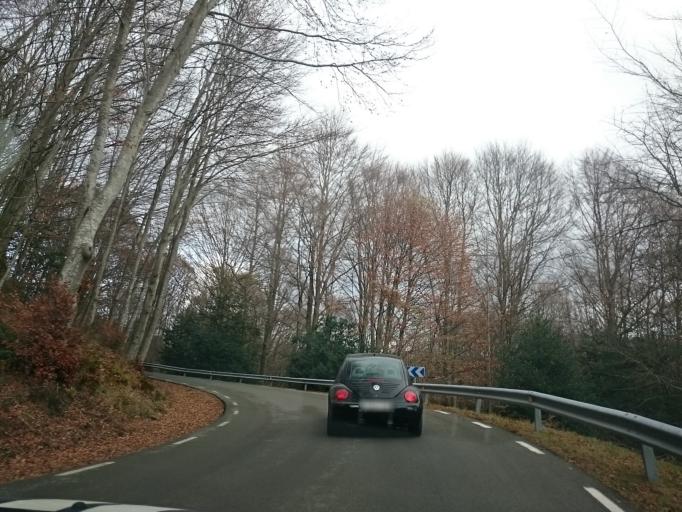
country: ES
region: Catalonia
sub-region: Provincia de Barcelona
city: Fogars de Montclus
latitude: 41.7652
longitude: 2.4667
